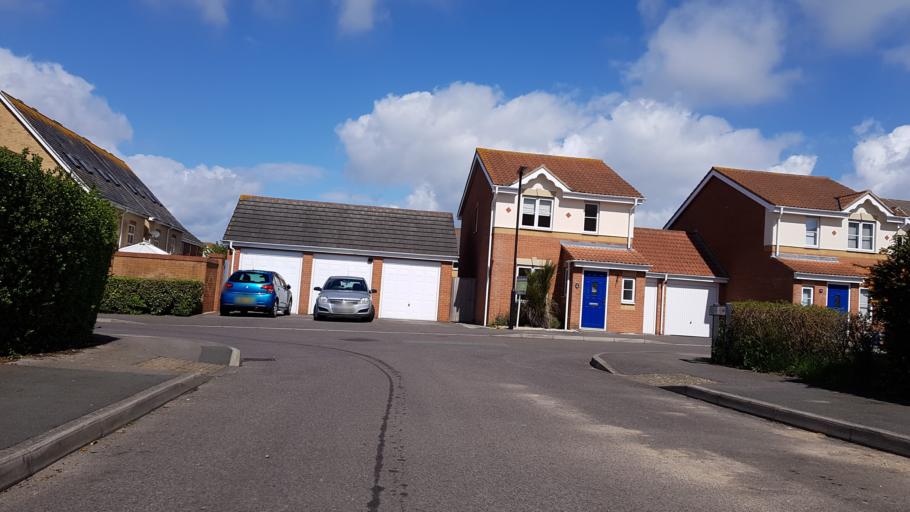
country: GB
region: England
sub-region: Isle of Wight
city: East Cowes
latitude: 50.7567
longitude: -1.2767
